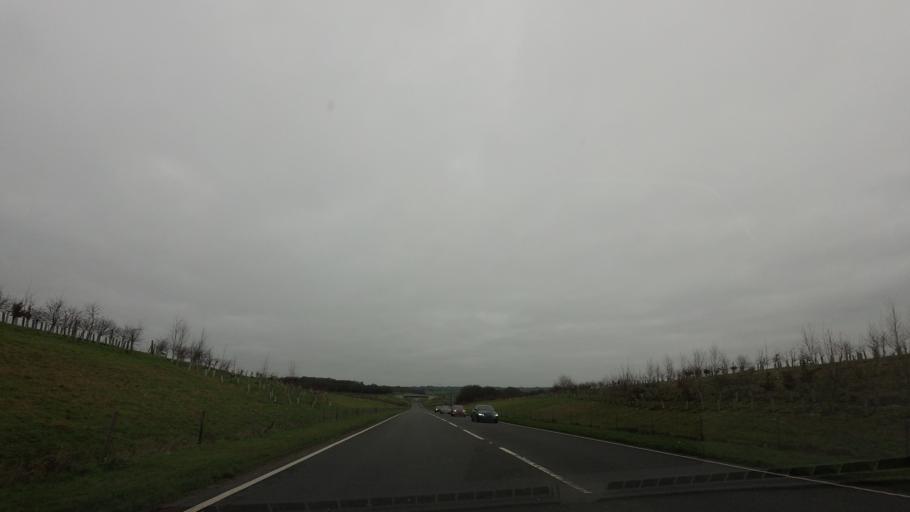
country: GB
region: England
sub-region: East Sussex
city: Bexhill-on-Sea
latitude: 50.8600
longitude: 0.4814
